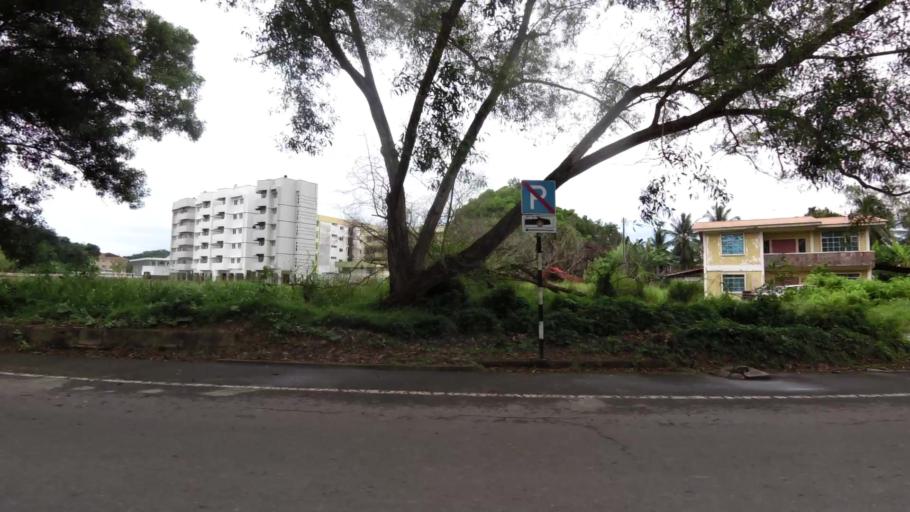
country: BN
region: Brunei and Muara
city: Bandar Seri Begawan
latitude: 4.8917
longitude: 114.9386
